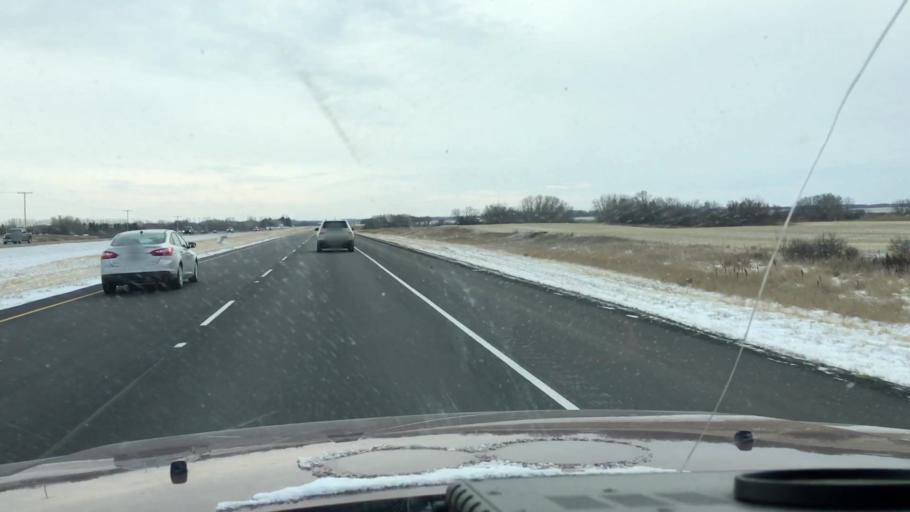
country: CA
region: Saskatchewan
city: Saskatoon
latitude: 52.0253
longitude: -106.5809
